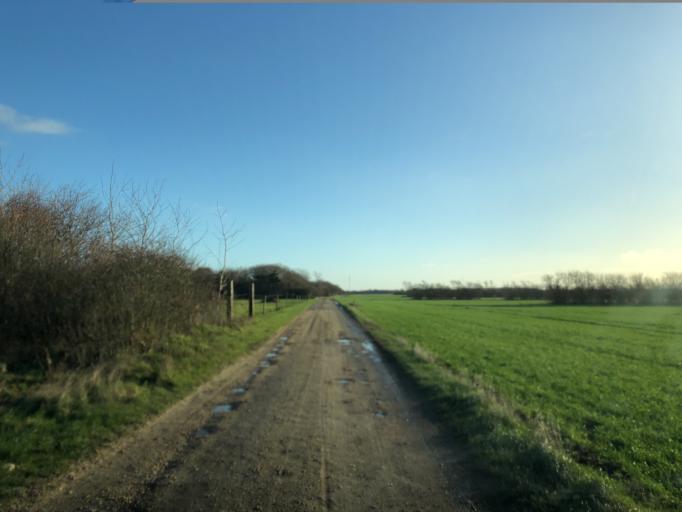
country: DK
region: Central Jutland
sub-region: Ringkobing-Skjern Kommune
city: Ringkobing
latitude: 56.1491
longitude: 8.2493
